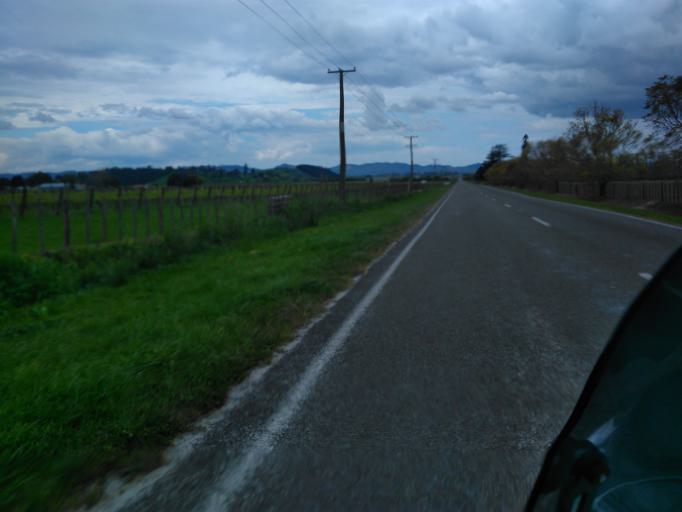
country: NZ
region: Gisborne
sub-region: Gisborne District
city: Gisborne
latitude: -38.6449
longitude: 177.8627
